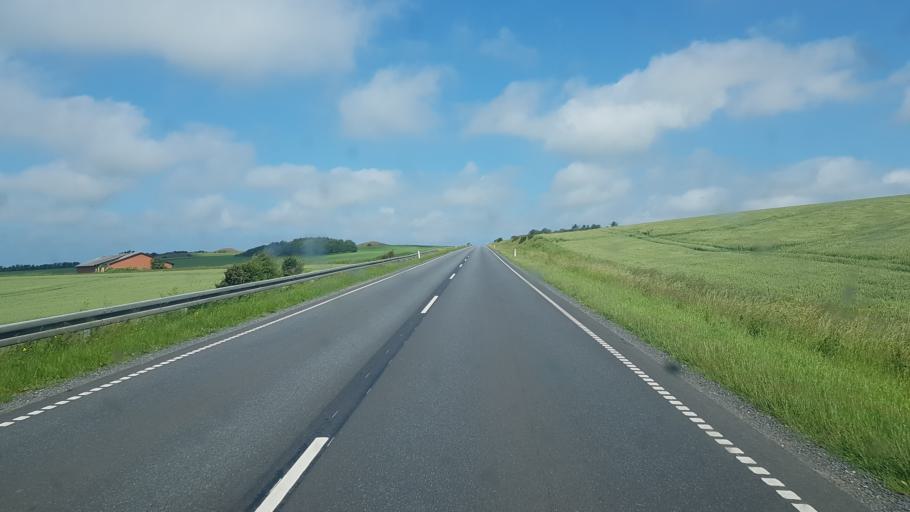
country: DK
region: Central Jutland
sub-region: Lemvig Kommune
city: Harboore
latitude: 56.5763
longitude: 8.2080
